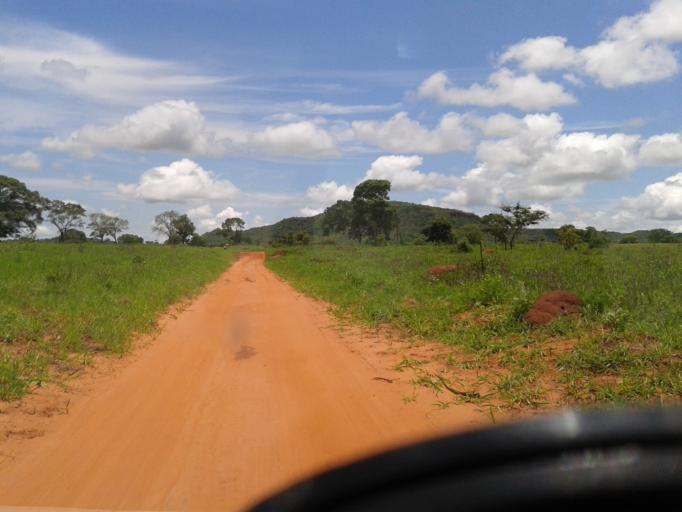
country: BR
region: Minas Gerais
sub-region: Santa Vitoria
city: Santa Vitoria
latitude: -18.9932
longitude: -49.9073
